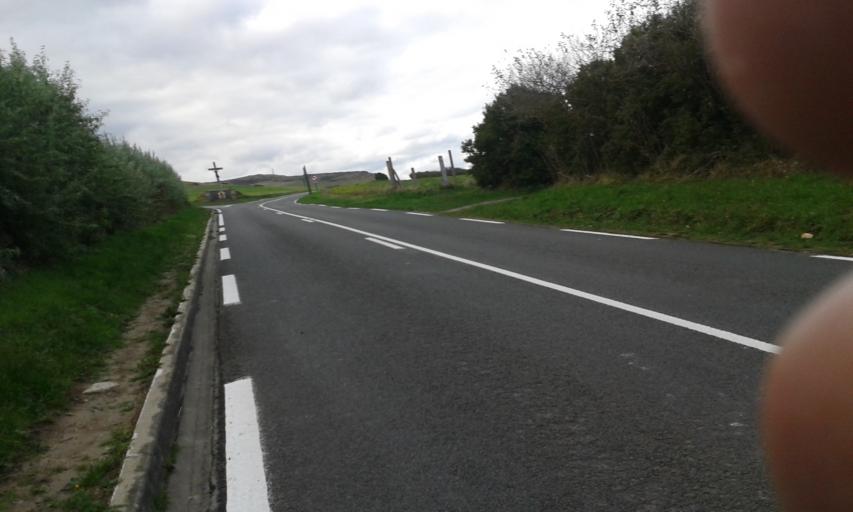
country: FR
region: Nord-Pas-de-Calais
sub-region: Departement du Pas-de-Calais
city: Sangatte
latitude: 50.9403
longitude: 1.7389
